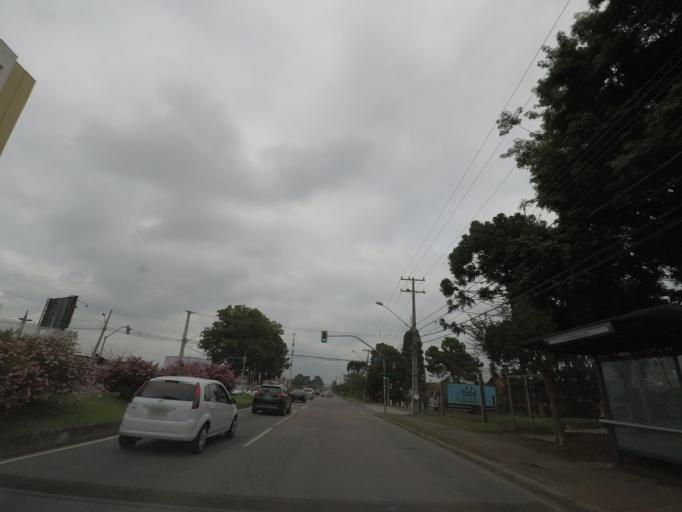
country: BR
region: Parana
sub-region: Curitiba
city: Curitiba
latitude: -25.4969
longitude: -49.3259
